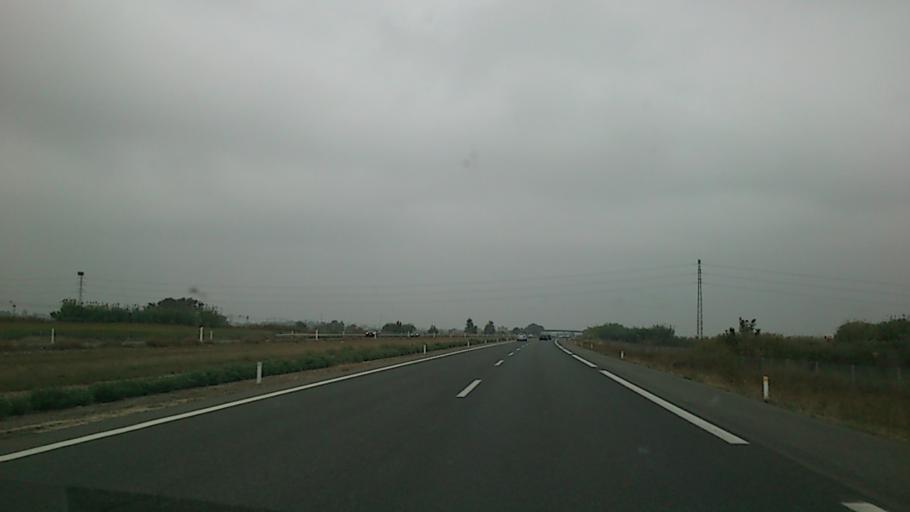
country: ES
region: Aragon
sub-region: Provincia de Zaragoza
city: Sobradiel
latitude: 41.7364
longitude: -1.0431
